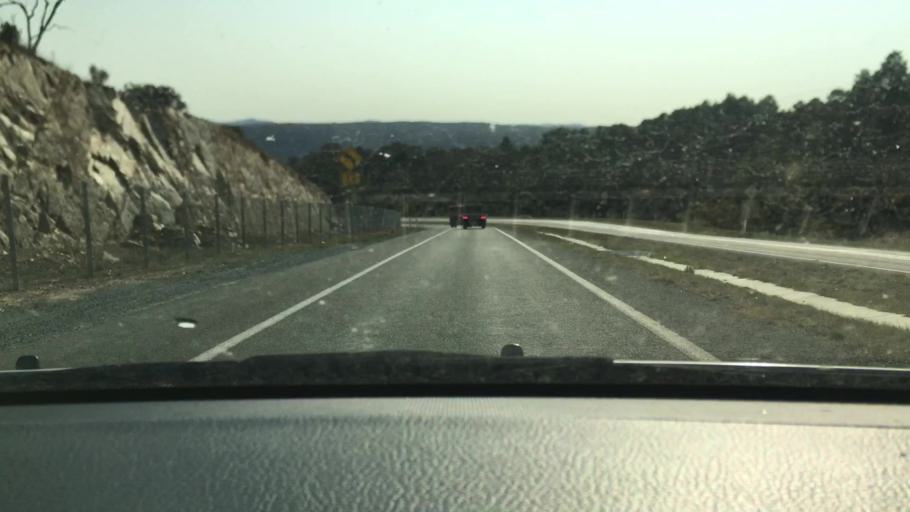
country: AU
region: New South Wales
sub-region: Queanbeyan
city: Queanbeyan
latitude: -35.3994
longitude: 149.2314
